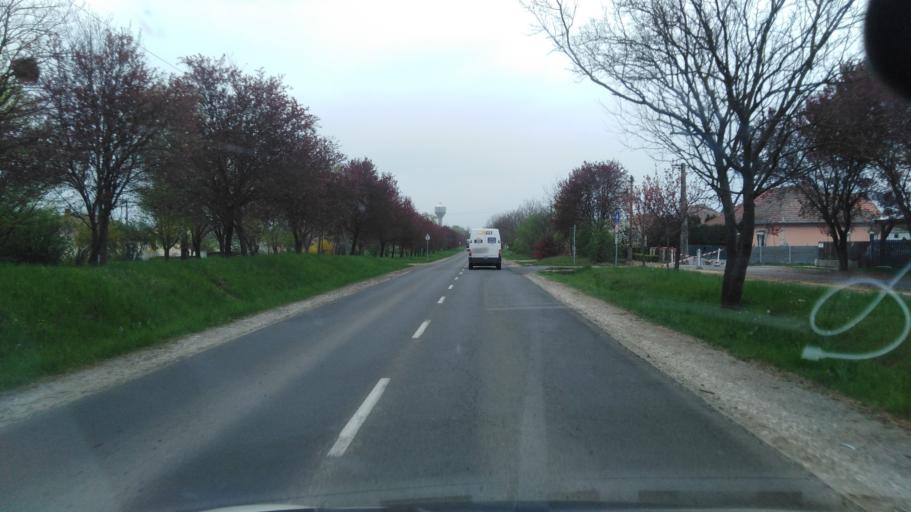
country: HU
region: Nograd
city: Balassagyarmat
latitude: 48.0640
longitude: 19.3019
